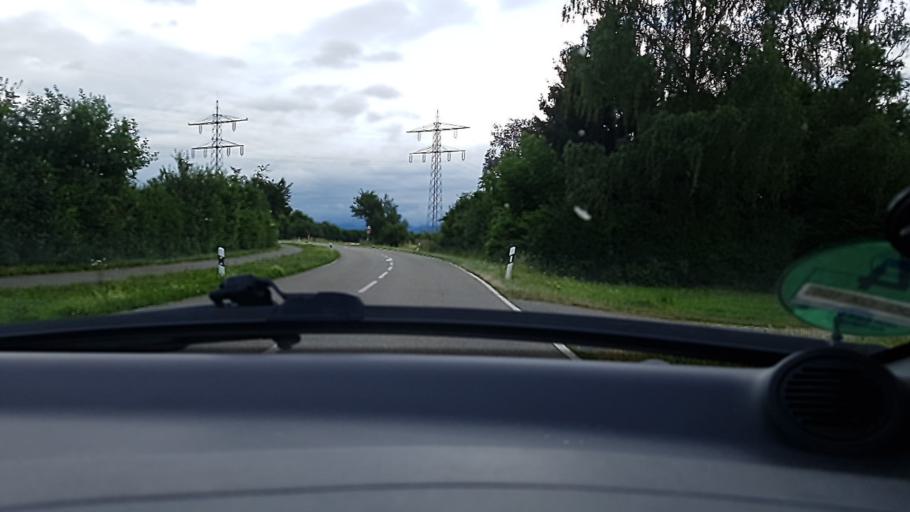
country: DE
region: Baden-Wuerttemberg
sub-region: Freiburg Region
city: Willstatt
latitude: 48.5337
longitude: 7.8817
